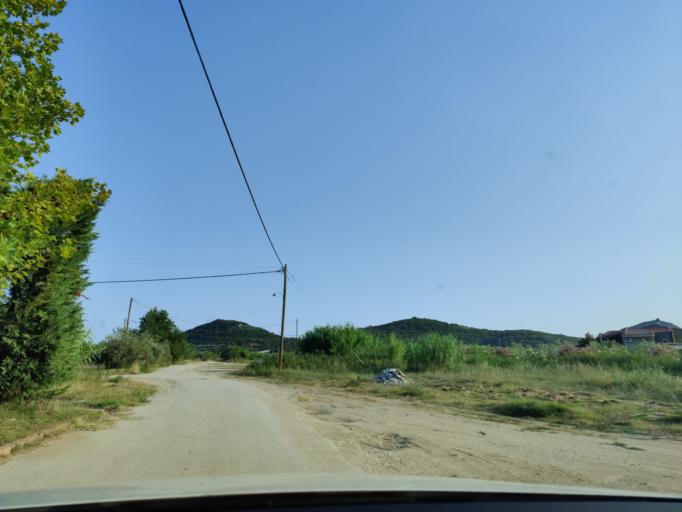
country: GR
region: East Macedonia and Thrace
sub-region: Nomos Kavalas
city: Nea Peramos
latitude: 40.8308
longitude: 24.3030
